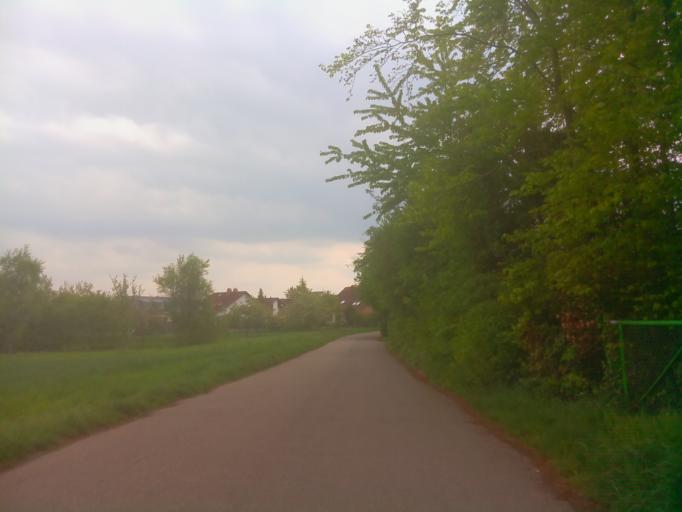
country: DE
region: Baden-Wuerttemberg
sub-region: Karlsruhe Region
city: Plankstadt
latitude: 49.3989
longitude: 8.5917
